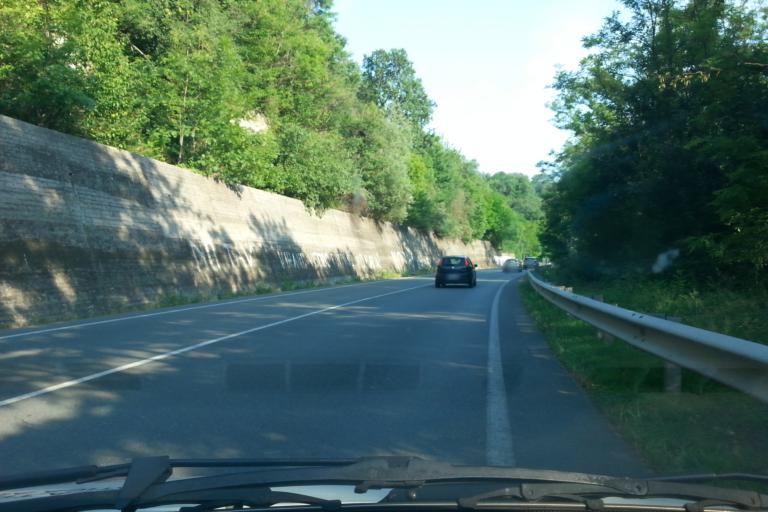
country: IT
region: Piedmont
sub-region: Provincia di Torino
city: Sant'Ambrogio di Torino
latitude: 45.1088
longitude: 7.3702
